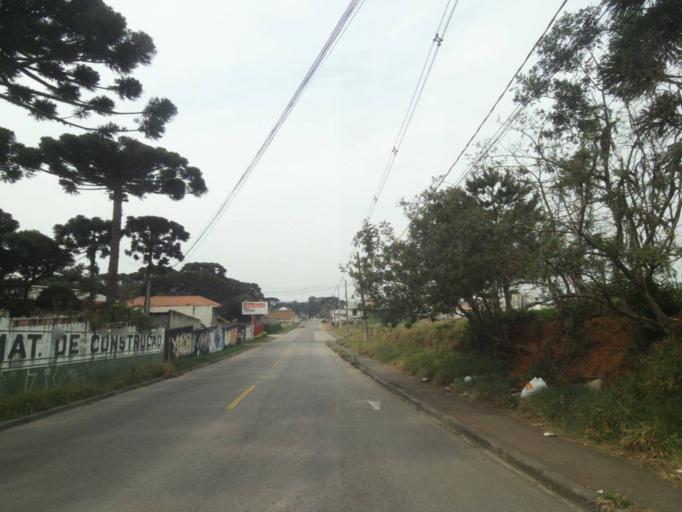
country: BR
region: Parana
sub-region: Sao Jose Dos Pinhais
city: Sao Jose dos Pinhais
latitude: -25.5281
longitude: -49.2815
